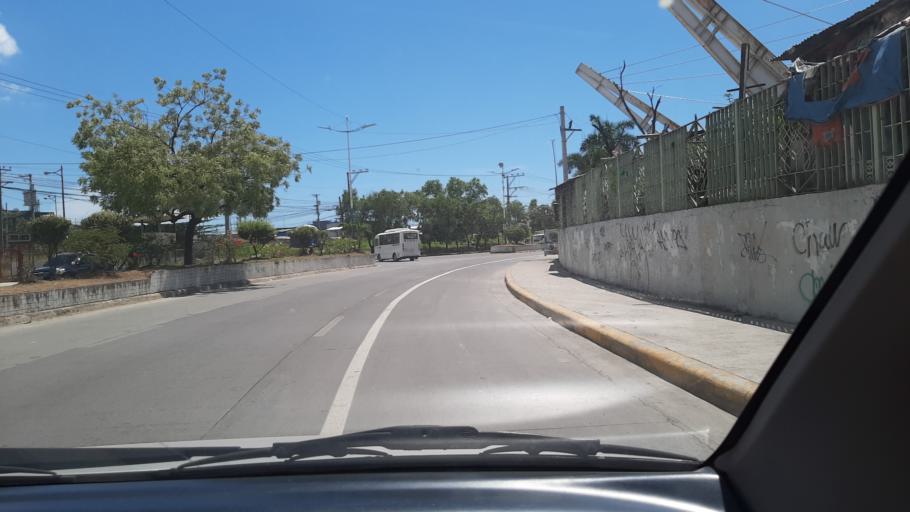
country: PH
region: Central Visayas
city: Mandaue City
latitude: 10.3275
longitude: 123.9359
